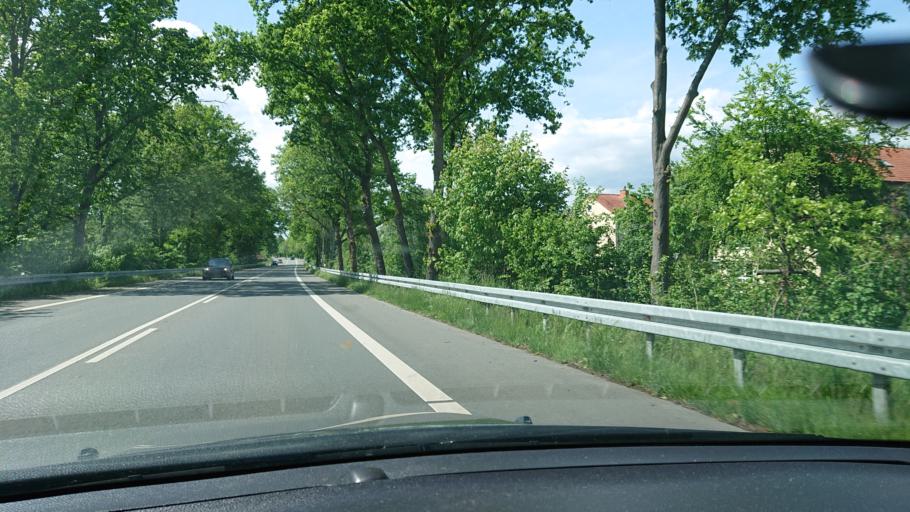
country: DE
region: North Rhine-Westphalia
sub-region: Regierungsbezirk Arnsberg
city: Hamm
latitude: 51.6720
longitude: 7.8410
